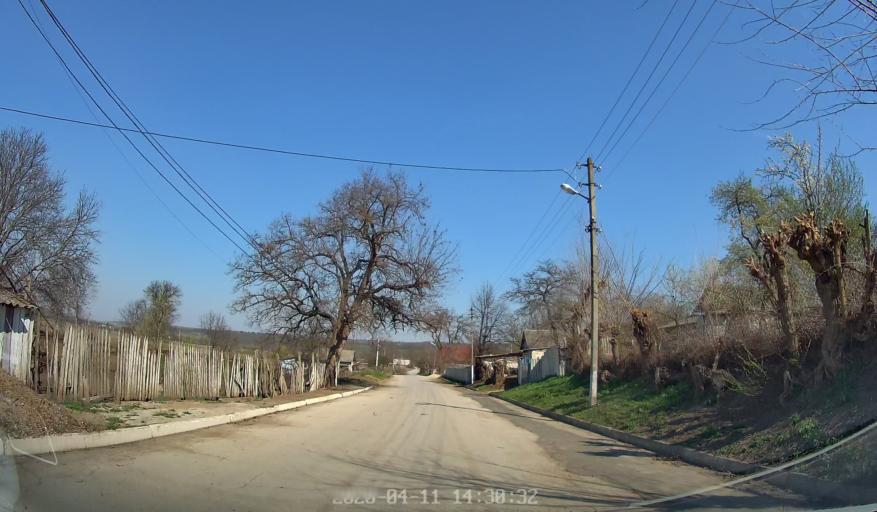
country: MD
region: Chisinau
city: Vadul lui Voda
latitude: 47.0987
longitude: 29.1601
